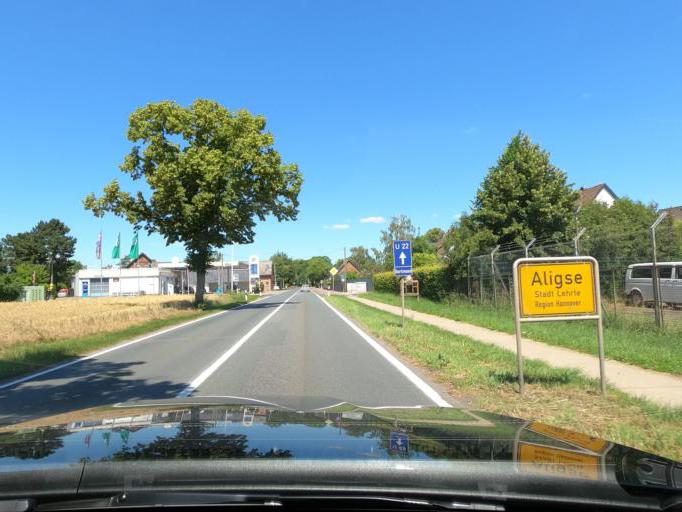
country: DE
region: Lower Saxony
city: Lehrte
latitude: 52.3975
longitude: 9.9740
